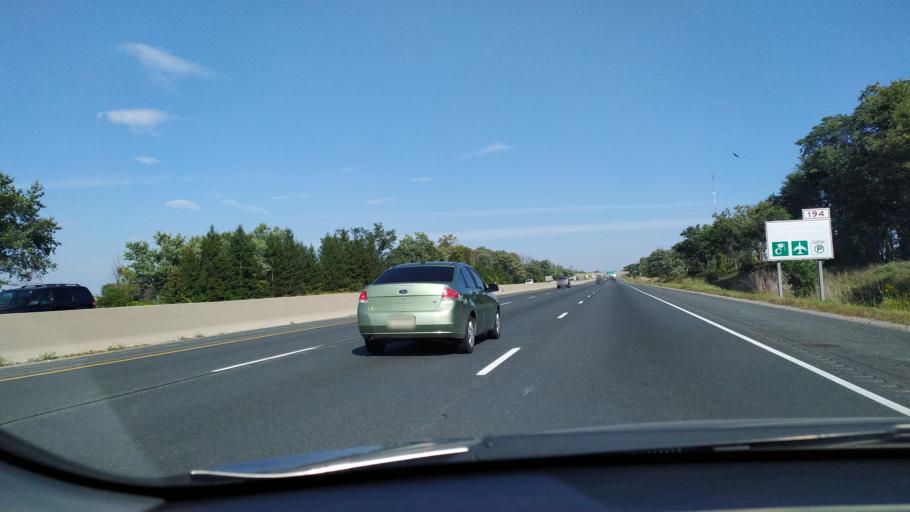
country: CA
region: Ontario
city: Dorchester
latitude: 42.9408
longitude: -81.1477
